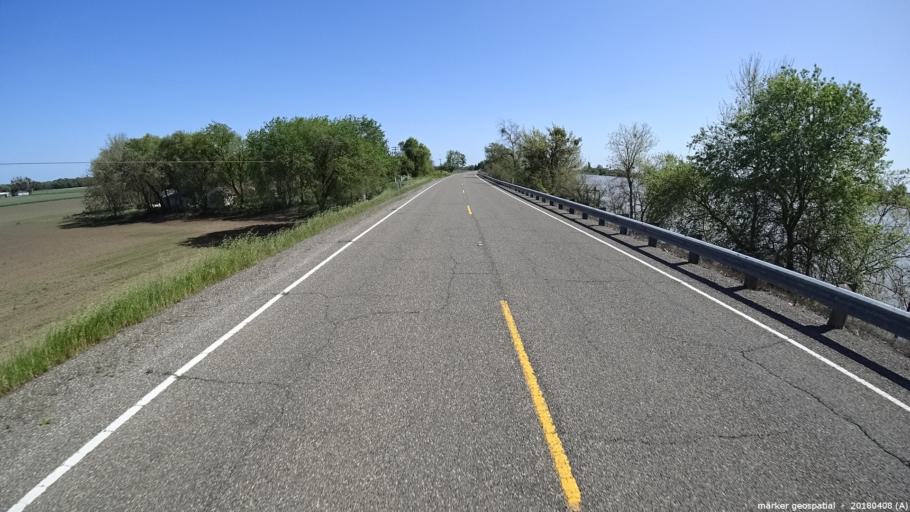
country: US
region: California
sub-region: Sacramento County
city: Laguna
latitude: 38.4117
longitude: -121.5178
